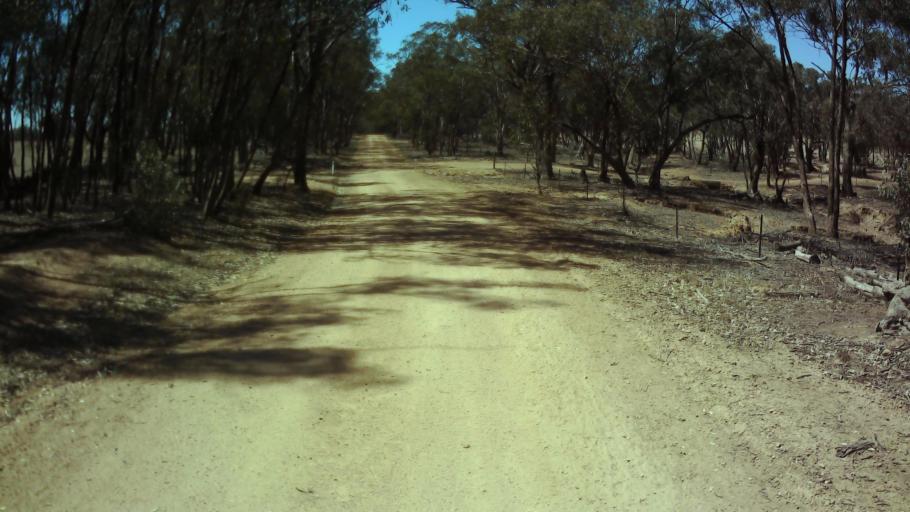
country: AU
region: New South Wales
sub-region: Weddin
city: Grenfell
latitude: -33.9596
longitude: 148.0866
